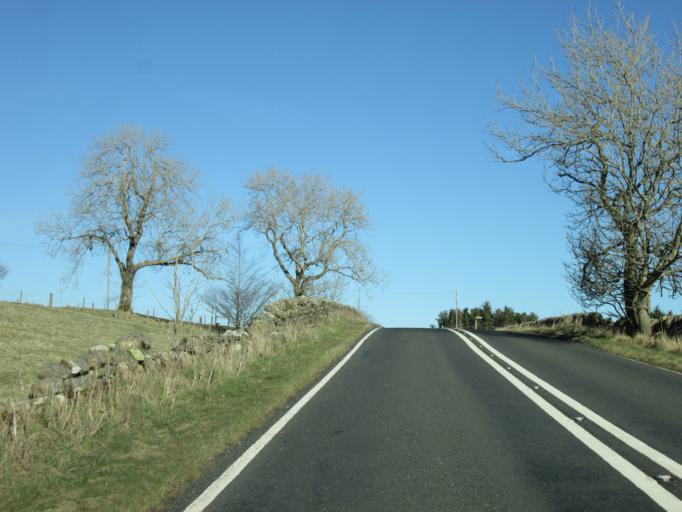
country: GB
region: England
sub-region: Northumberland
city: Birtley
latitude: 55.0362
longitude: -2.2160
